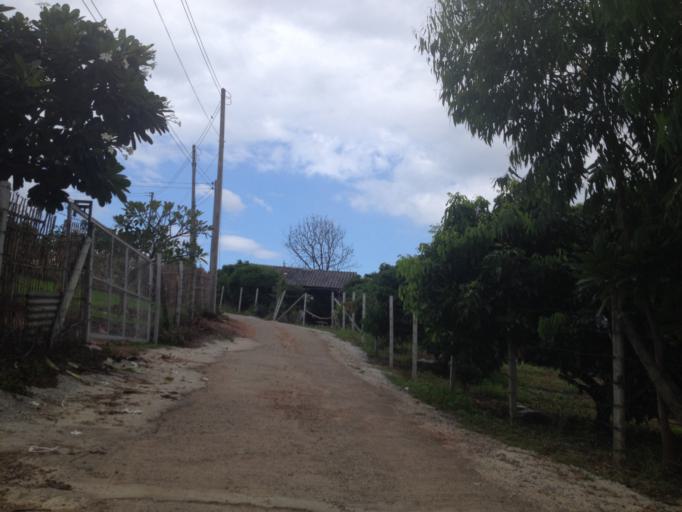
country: TH
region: Chiang Mai
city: Hang Dong
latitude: 18.6938
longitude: 98.8810
